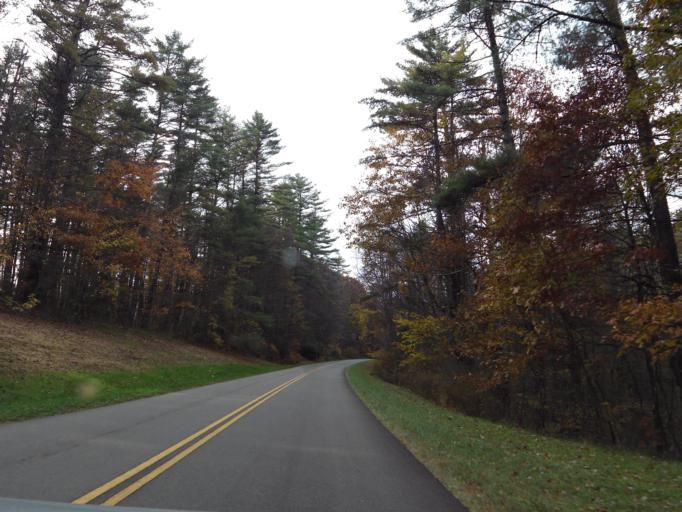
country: US
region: North Carolina
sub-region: Wilkes County
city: Mulberry
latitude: 36.3886
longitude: -81.2616
